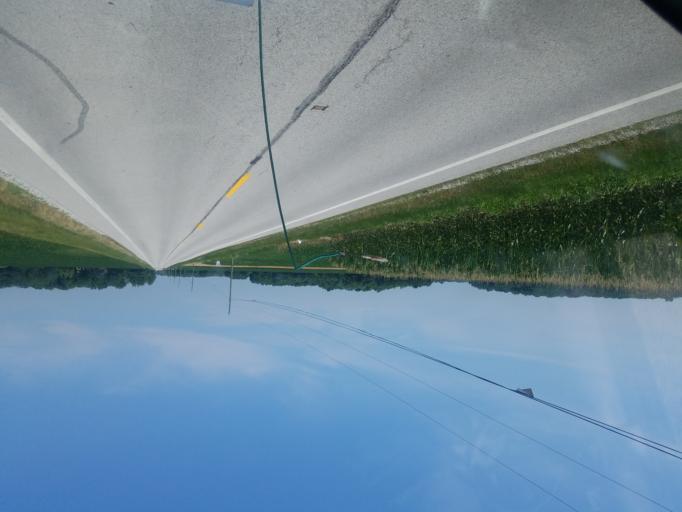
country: US
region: Ohio
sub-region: Auglaize County
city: New Bremen
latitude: 40.4816
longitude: -84.4345
